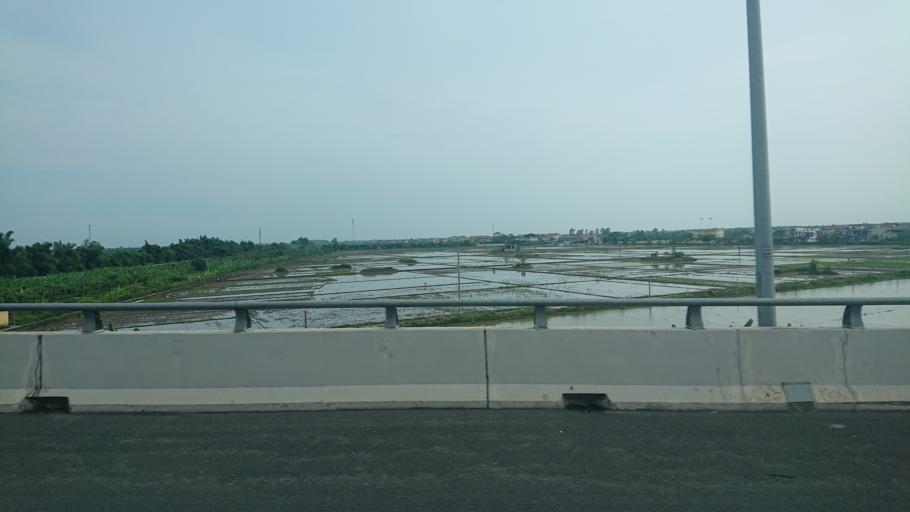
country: VN
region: Hai Duong
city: Tu Ky
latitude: 20.8338
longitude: 106.4393
